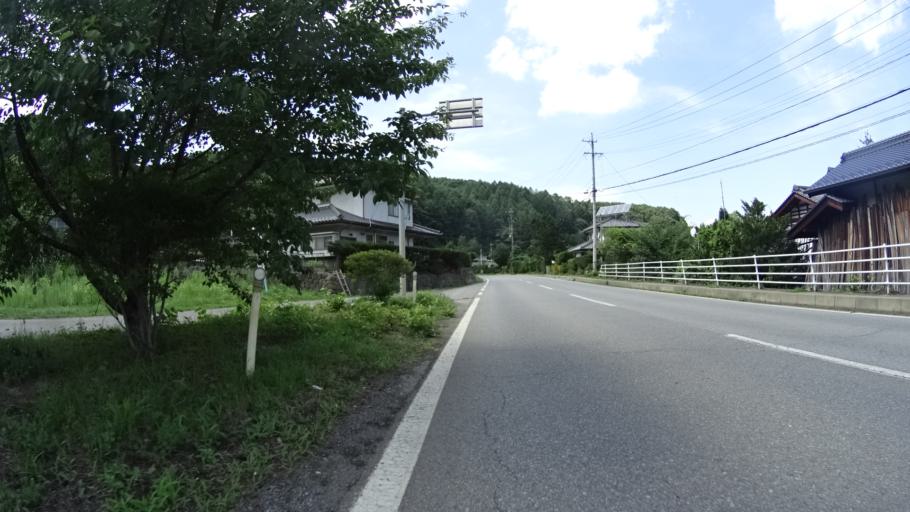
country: JP
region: Nagano
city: Saku
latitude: 36.0781
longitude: 138.4900
